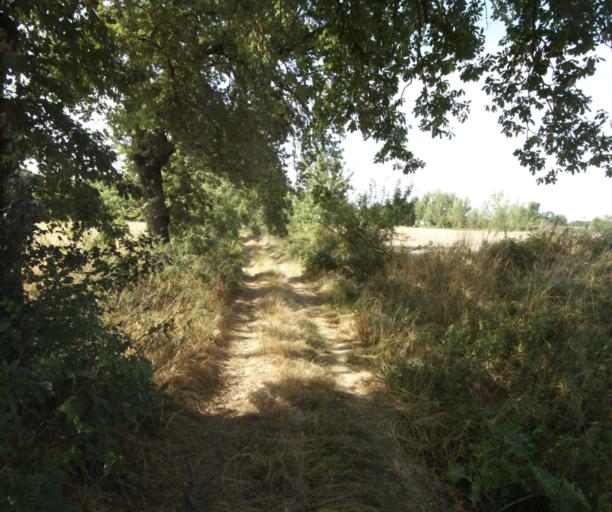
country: FR
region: Midi-Pyrenees
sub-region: Departement du Tarn
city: Soual
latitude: 43.5285
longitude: 2.0787
